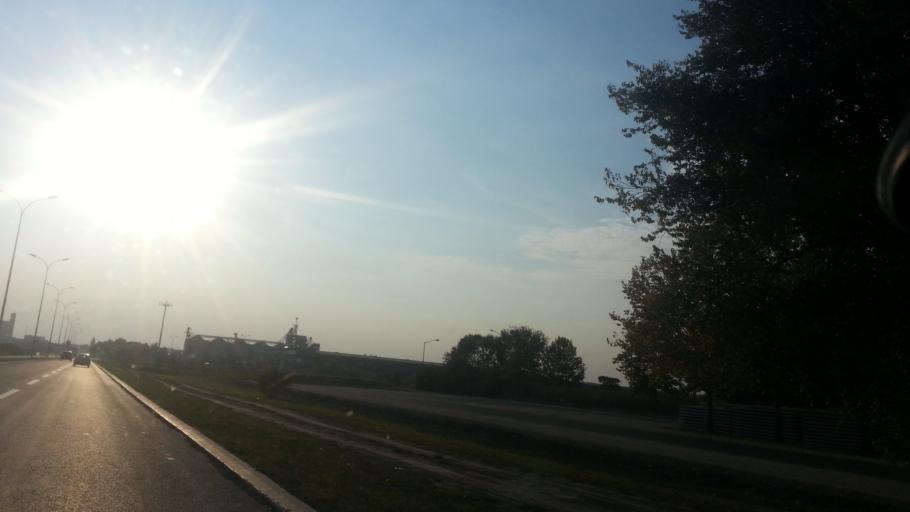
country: RS
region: Autonomna Pokrajina Vojvodina
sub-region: Sremski Okrug
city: Ingija
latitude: 45.0571
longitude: 20.1078
